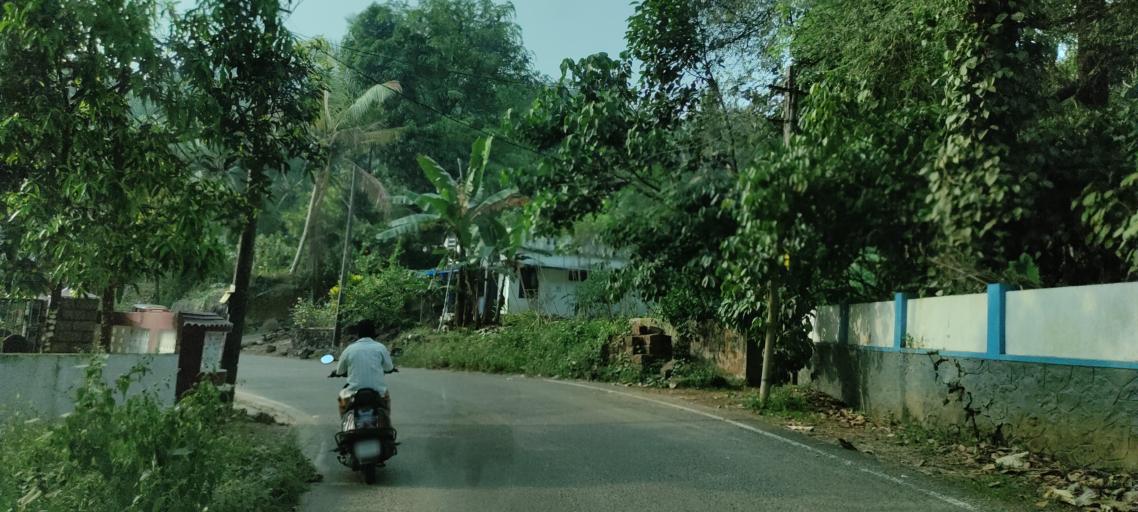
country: IN
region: Kerala
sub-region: Ernakulam
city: Piravam
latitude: 9.8017
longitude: 76.5051
